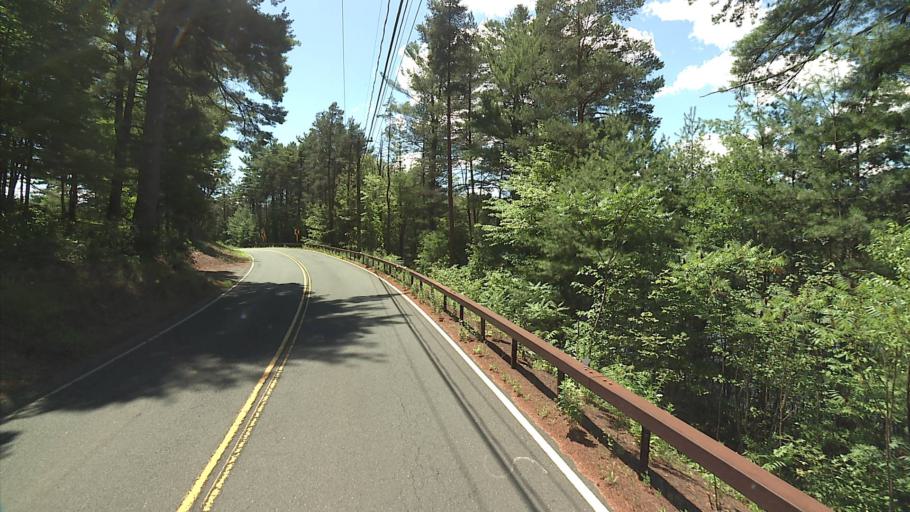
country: US
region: Connecticut
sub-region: Litchfield County
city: New Hartford Center
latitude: 41.8959
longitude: -72.9578
